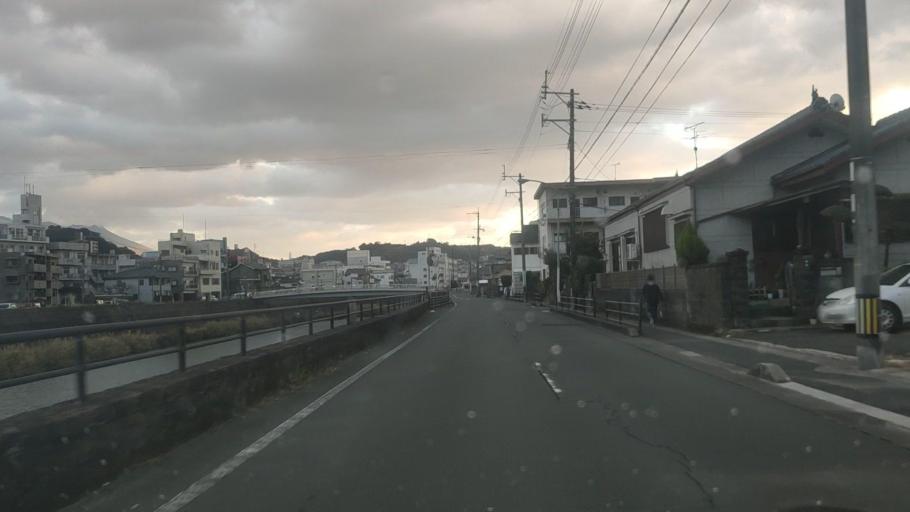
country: JP
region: Kagoshima
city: Kagoshima-shi
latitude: 31.6115
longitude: 130.5308
